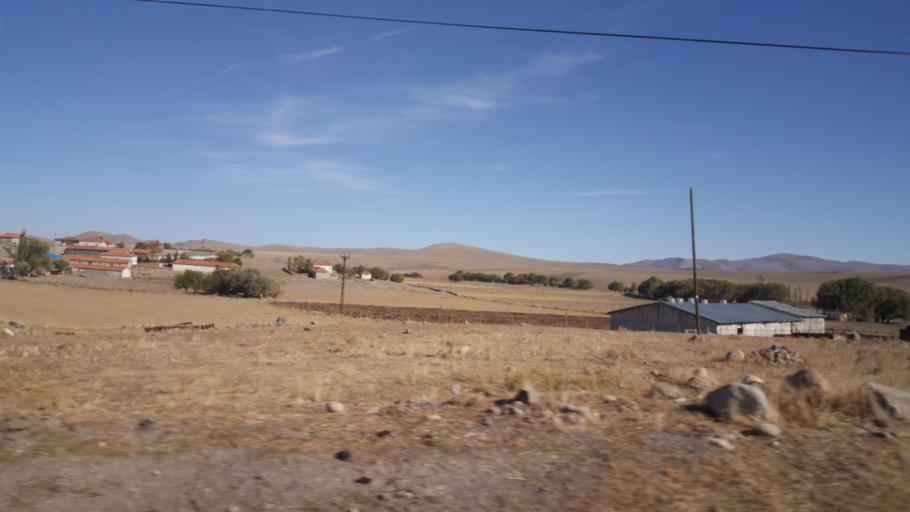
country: TR
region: Ankara
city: Altpinar
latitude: 39.2412
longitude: 32.7433
